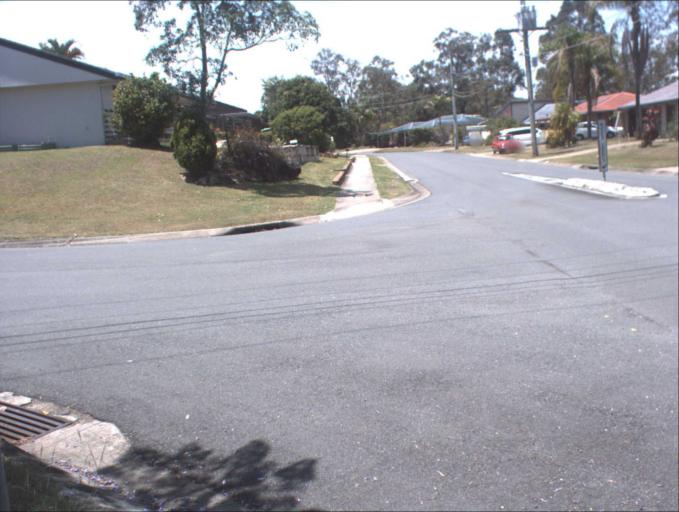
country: AU
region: Queensland
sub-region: Logan
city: Slacks Creek
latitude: -27.6394
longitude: 153.1415
